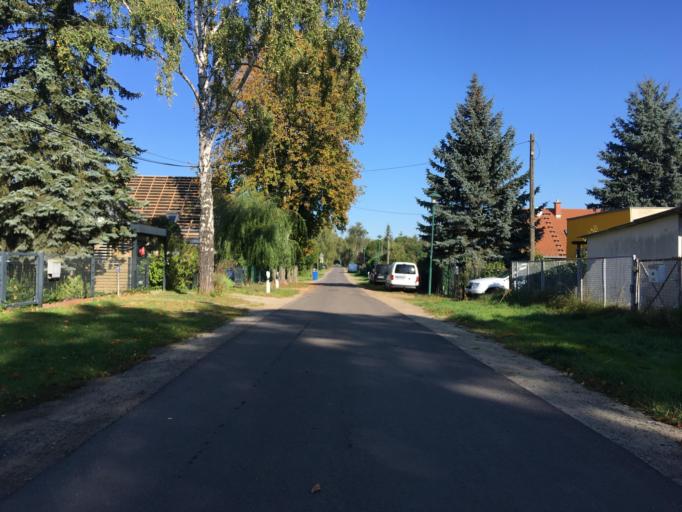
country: DE
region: Berlin
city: Buch
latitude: 52.6688
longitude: 13.5213
